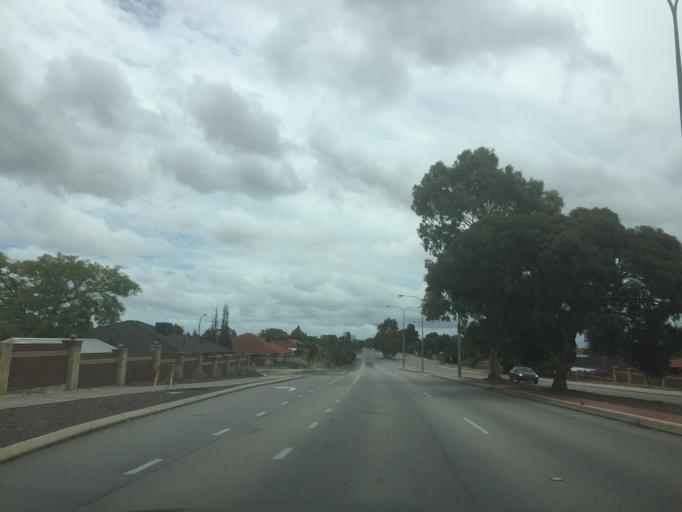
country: AU
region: Western Australia
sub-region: Gosnells
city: Thornlie
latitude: -32.0801
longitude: 115.9491
